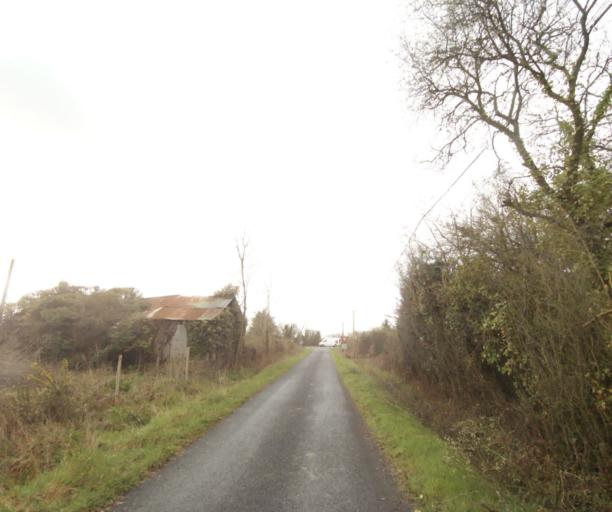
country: FR
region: Pays de la Loire
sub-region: Departement de la Loire-Atlantique
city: Bouvron
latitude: 47.3971
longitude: -1.8715
